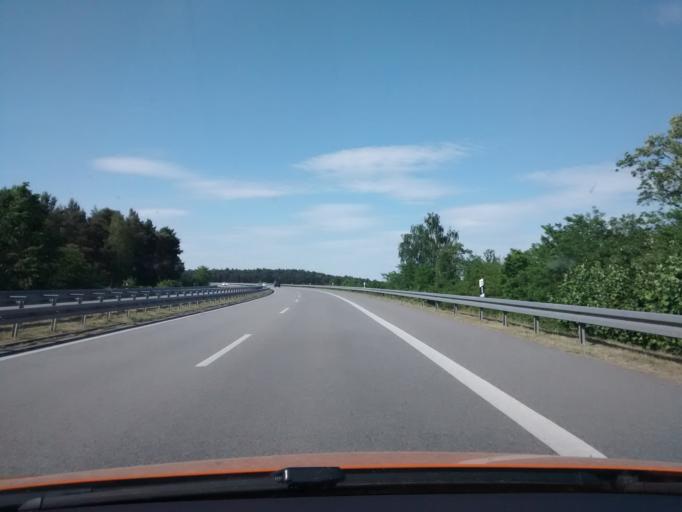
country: DE
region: Brandenburg
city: Trebbin
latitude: 52.1969
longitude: 13.2555
